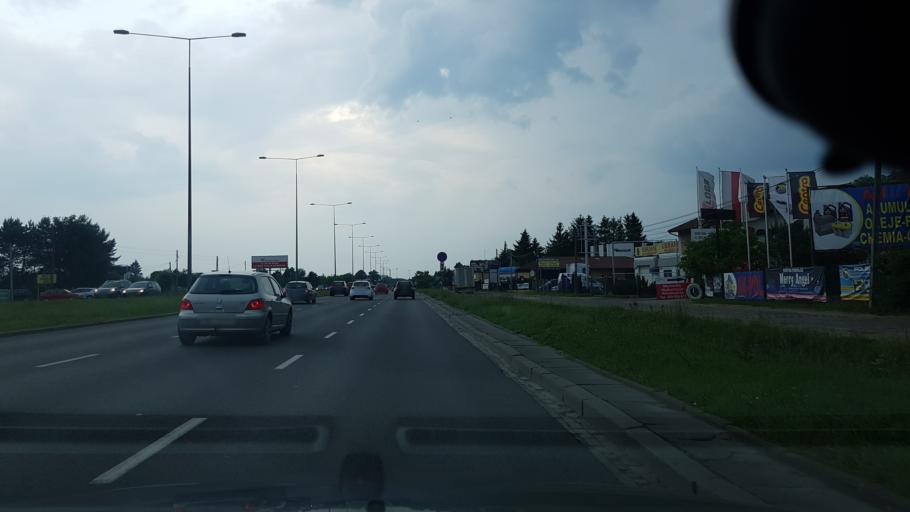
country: PL
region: Masovian Voivodeship
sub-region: Warszawa
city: Bialoleka
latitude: 52.3390
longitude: 20.9570
